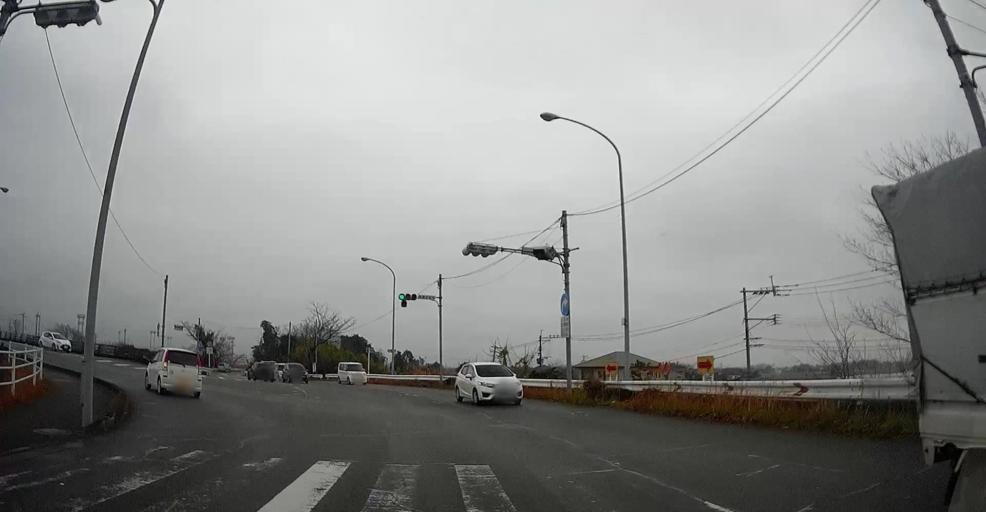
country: JP
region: Kumamoto
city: Kumamoto
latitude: 32.7610
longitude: 130.7525
